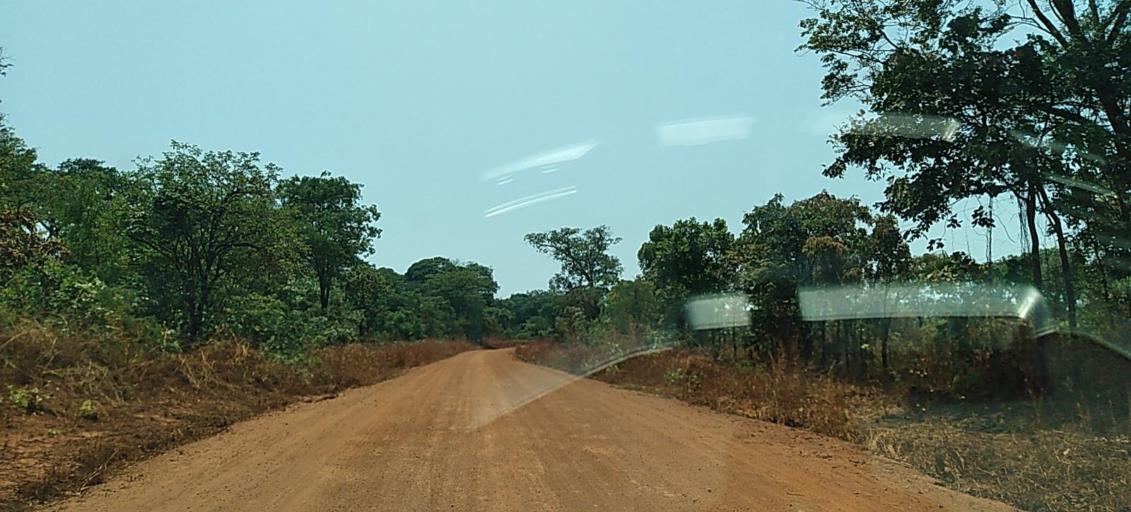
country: ZM
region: North-Western
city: Kansanshi
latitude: -11.9839
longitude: 26.8589
